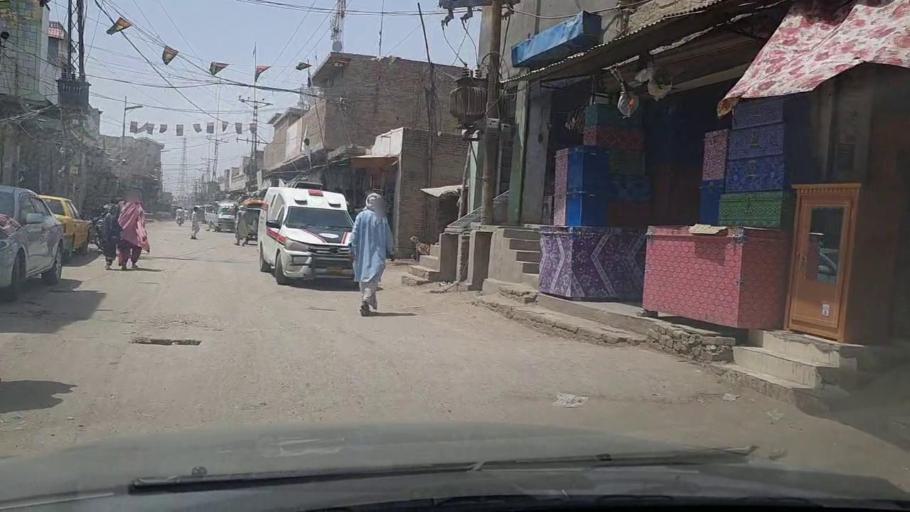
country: PK
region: Sindh
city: Miro Khan
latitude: 27.7610
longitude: 68.0949
